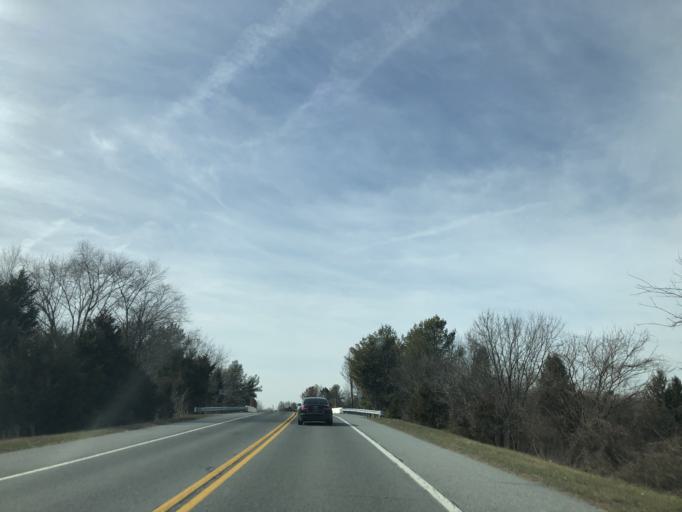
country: US
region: Delaware
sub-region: Kent County
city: Smyrna
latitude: 39.2915
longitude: -75.5918
